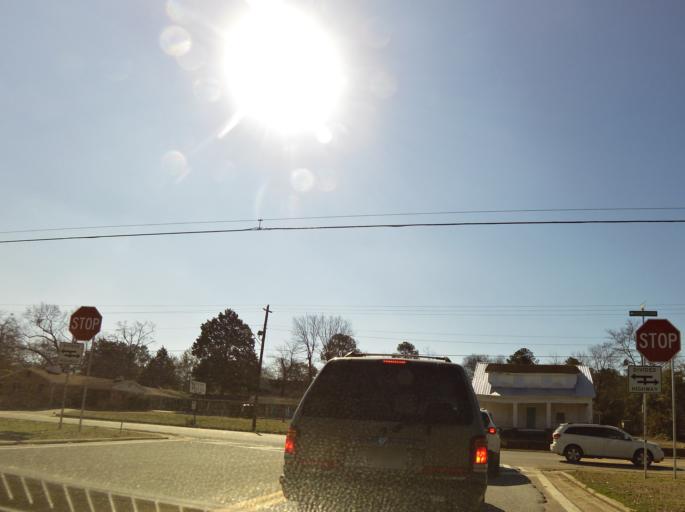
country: US
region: Georgia
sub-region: Pulaski County
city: Hawkinsville
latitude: 32.2815
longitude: -83.4790
